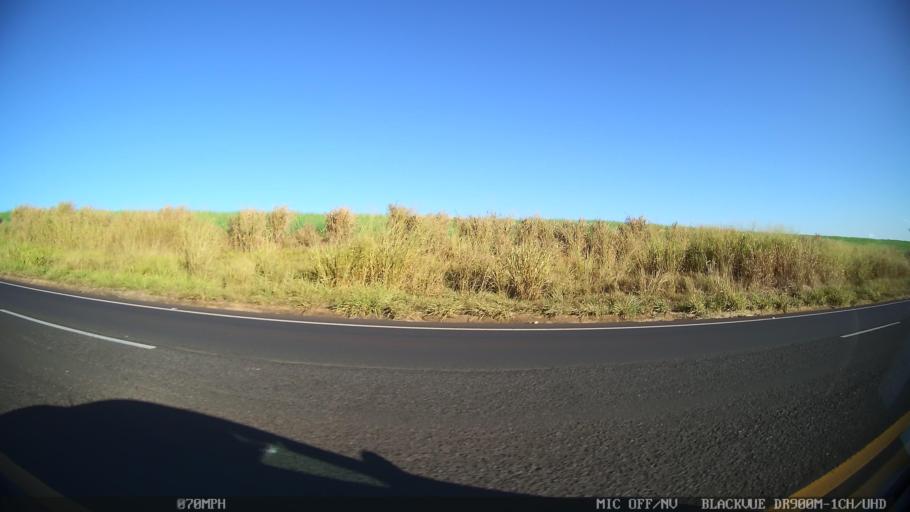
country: BR
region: Sao Paulo
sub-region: Guapiacu
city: Guapiacu
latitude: -20.7400
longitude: -49.0930
